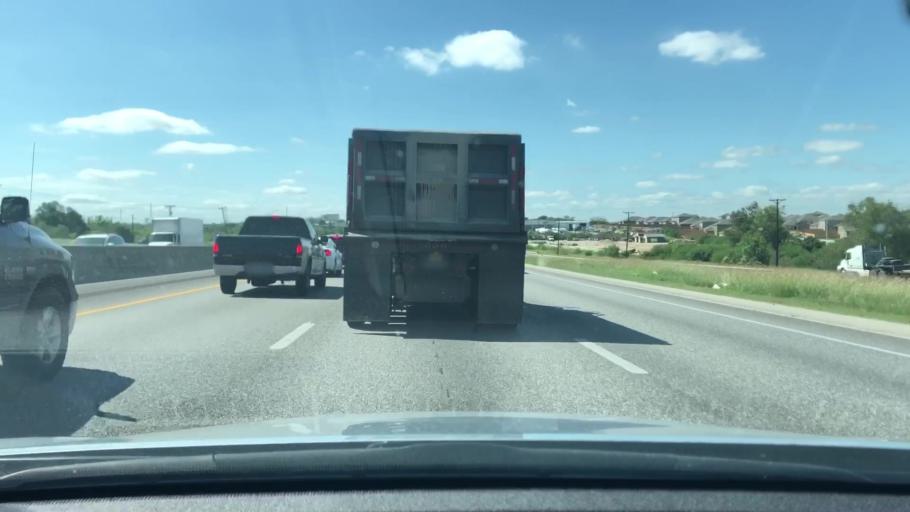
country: US
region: Texas
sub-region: Guadalupe County
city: Northcliff
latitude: 29.6523
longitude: -98.1912
